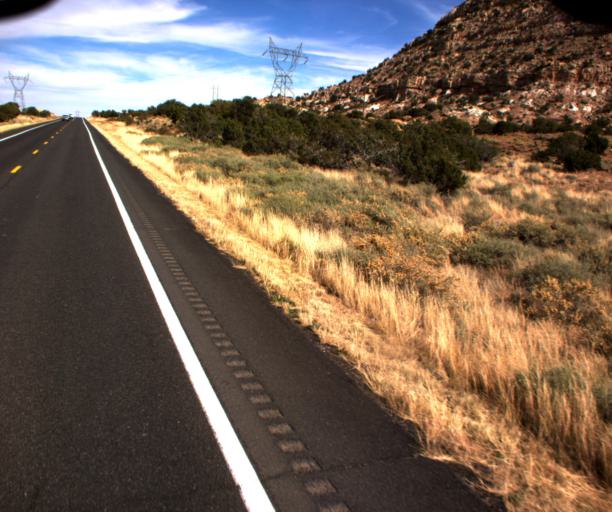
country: US
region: Arizona
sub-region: Navajo County
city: Kayenta
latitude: 36.6899
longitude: -110.3699
